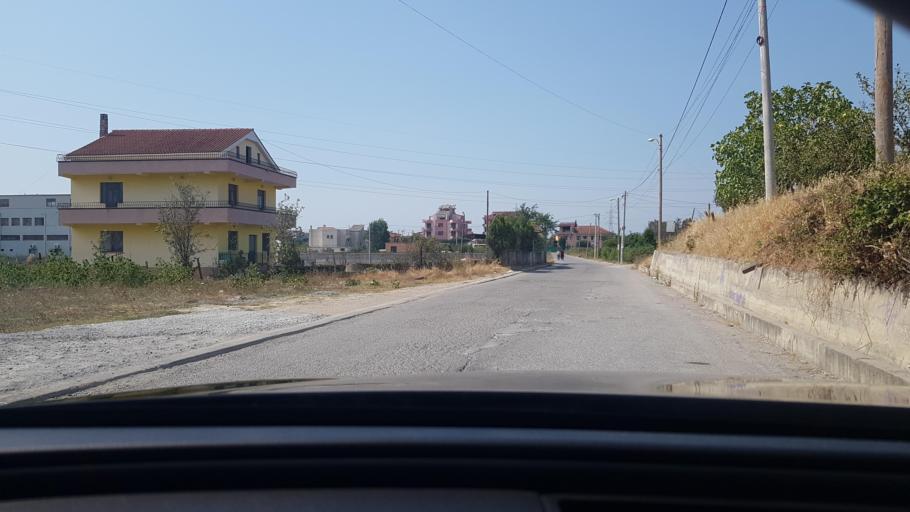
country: AL
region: Durres
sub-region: Rrethi i Durresit
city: Rrashbull
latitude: 41.3320
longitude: 19.5092
